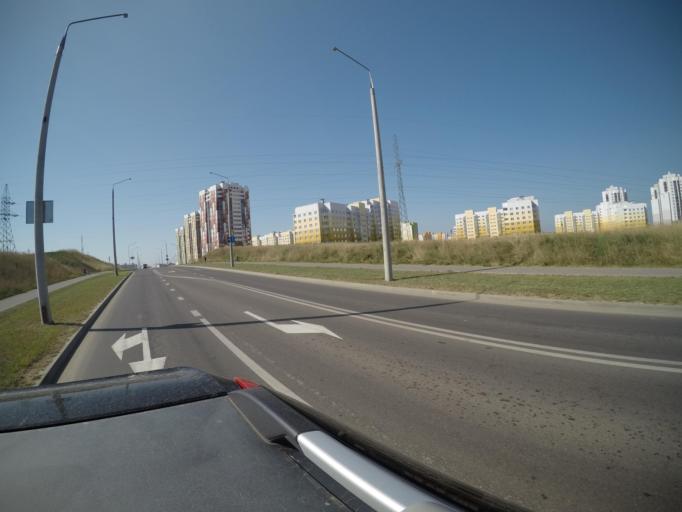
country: BY
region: Grodnenskaya
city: Hrodna
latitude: 53.7199
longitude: 23.8708
